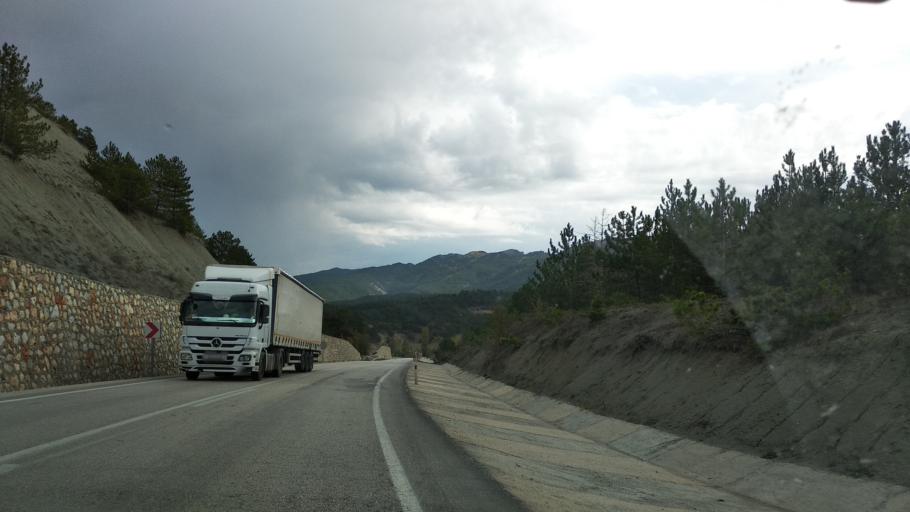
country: TR
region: Bolu
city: Mudurnu
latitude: 40.4375
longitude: 31.1519
